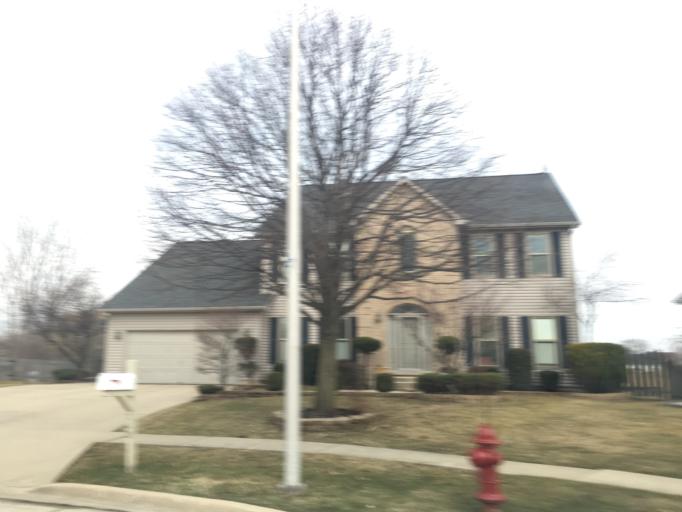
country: US
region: Illinois
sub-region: Cook County
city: Schaumburg
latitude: 42.0398
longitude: -88.1184
